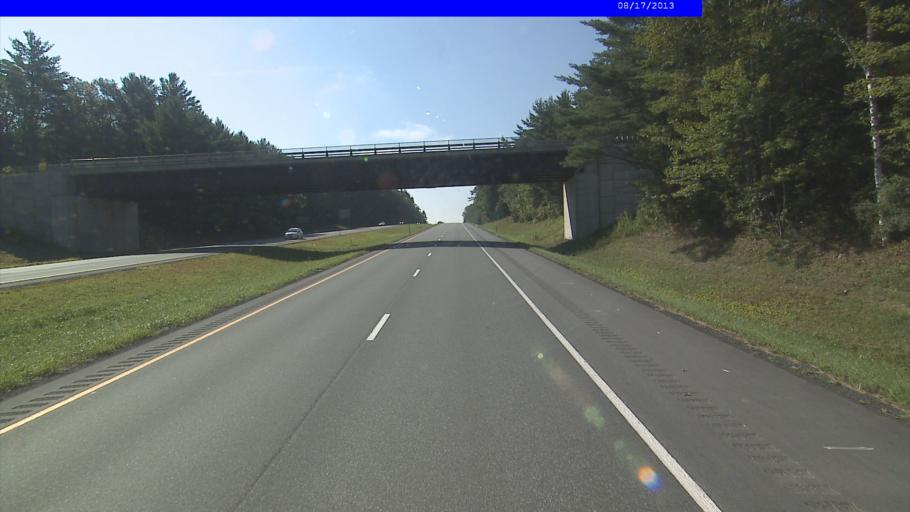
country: US
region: Vermont
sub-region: Windsor County
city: White River Junction
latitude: 43.6127
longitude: -72.3457
